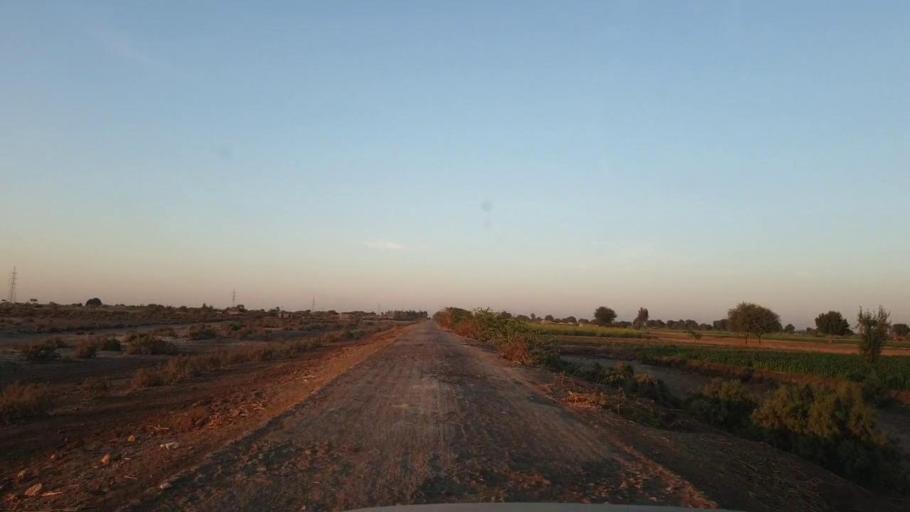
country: PK
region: Sindh
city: Kunri
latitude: 25.1399
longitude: 69.4444
